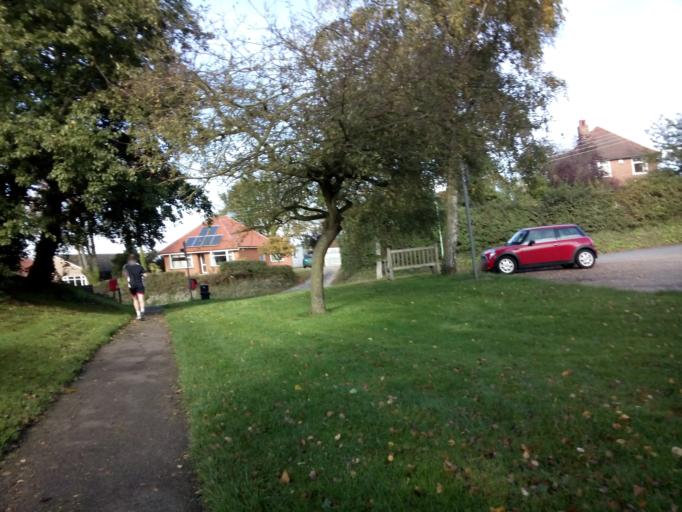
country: GB
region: England
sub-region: Suffolk
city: Hadleigh
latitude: 52.0411
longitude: 0.9596
